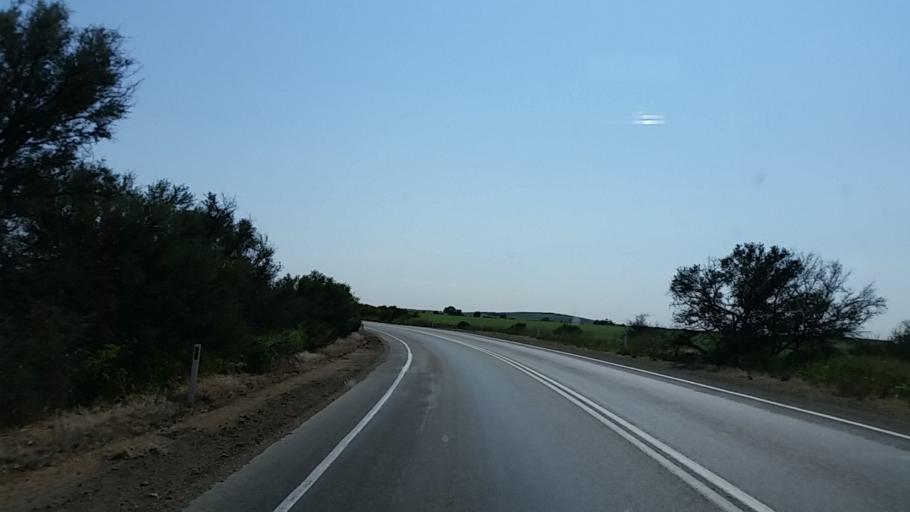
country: AU
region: South Australia
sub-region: Northern Areas
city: Jamestown
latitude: -33.2345
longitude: 138.3911
